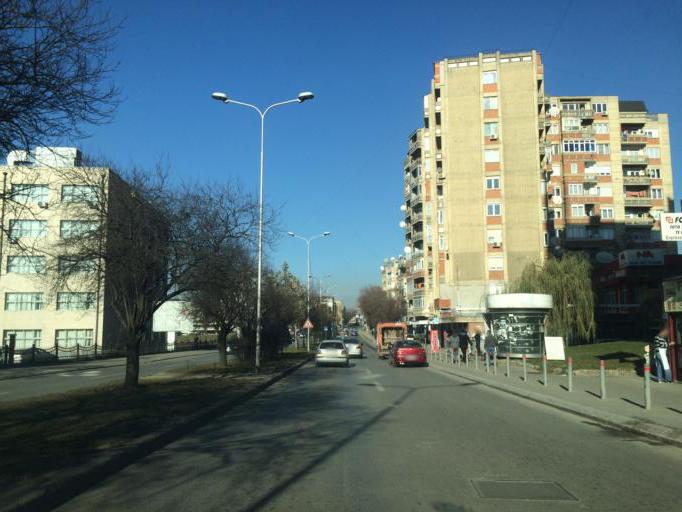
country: XK
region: Pristina
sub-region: Komuna e Prishtines
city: Pristina
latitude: 42.6569
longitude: 21.1644
